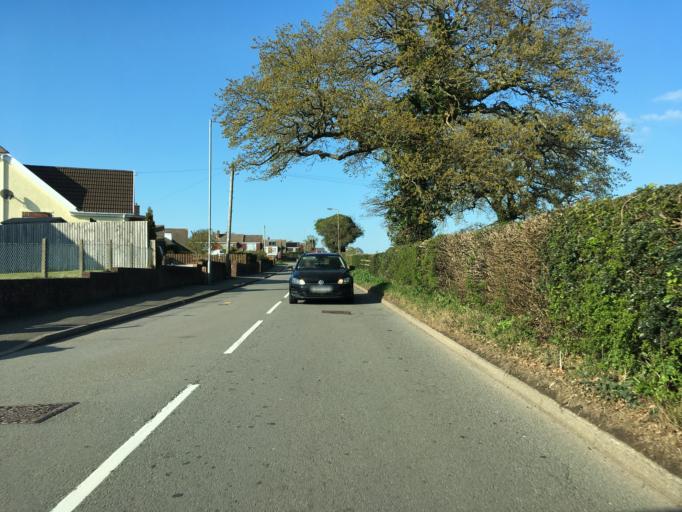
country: GB
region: Wales
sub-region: Torfaen County Borough
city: New Inn
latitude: 51.6913
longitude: -3.0018
